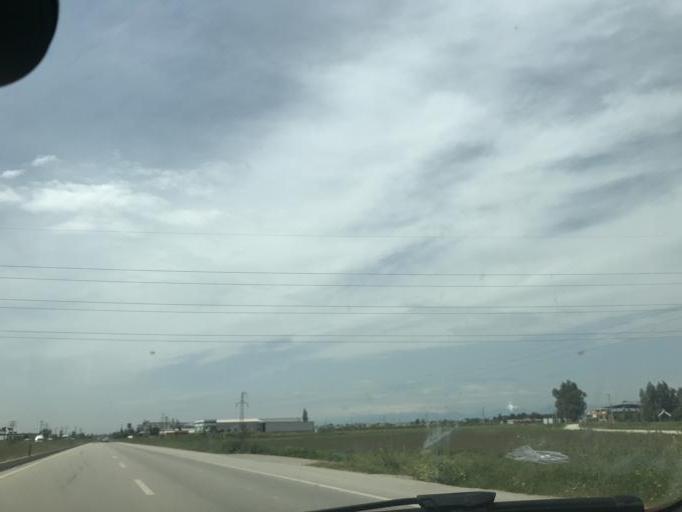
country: TR
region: Adana
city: Yuregir
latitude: 36.9794
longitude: 35.4563
